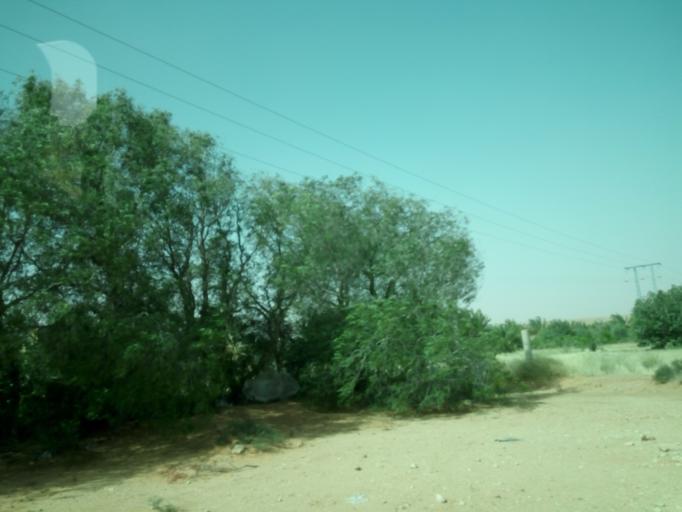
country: DZ
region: Ghardaia
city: Berriane
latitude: 32.8478
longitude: 3.9143
